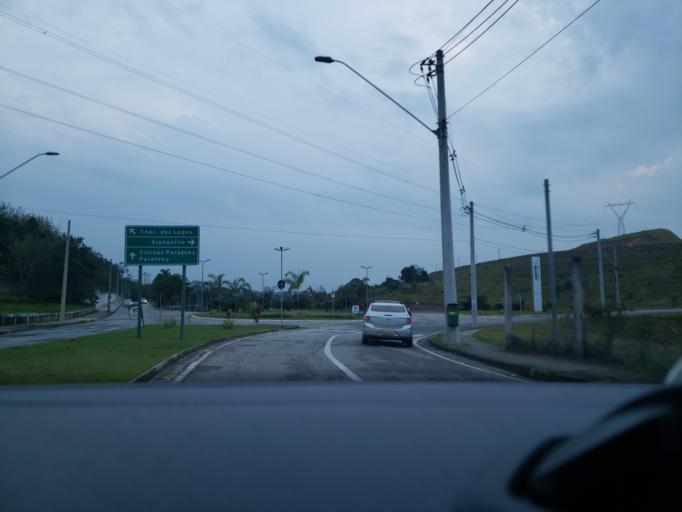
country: BR
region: Sao Paulo
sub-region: Sao Jose Dos Campos
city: Sao Jose dos Campos
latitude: -23.1919
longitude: -45.9363
